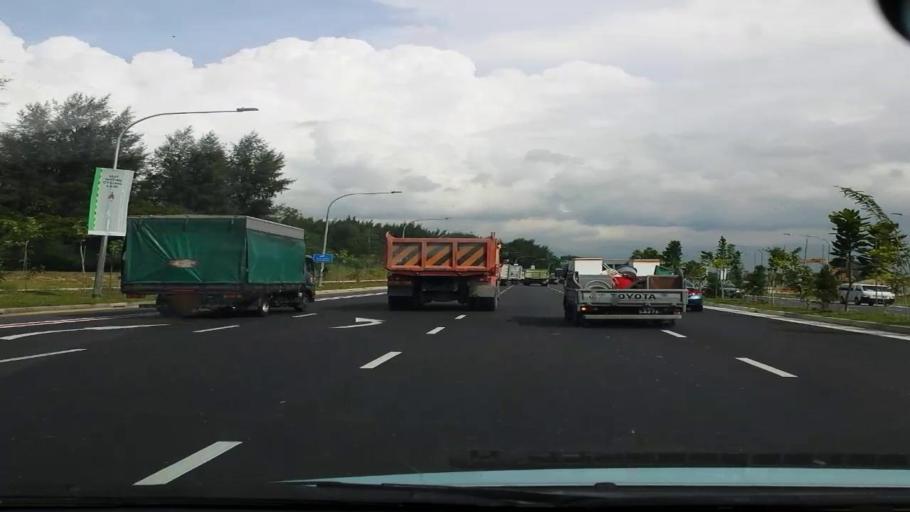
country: SG
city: Singapore
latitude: 1.3186
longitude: 103.9838
